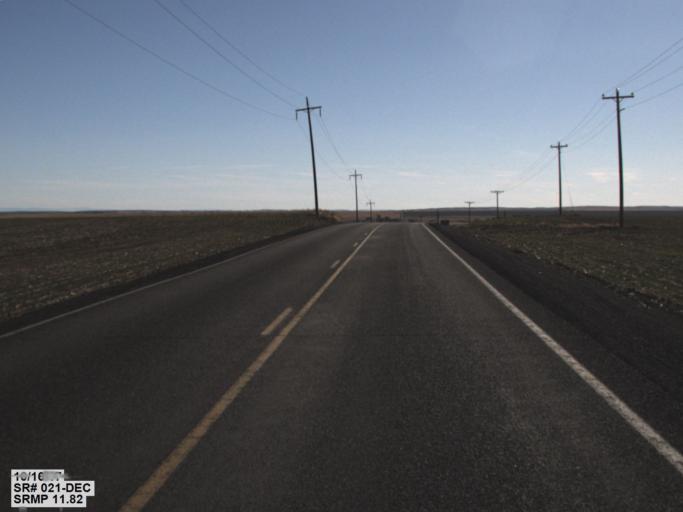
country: US
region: Washington
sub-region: Franklin County
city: Connell
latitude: 46.7974
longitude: -118.5473
